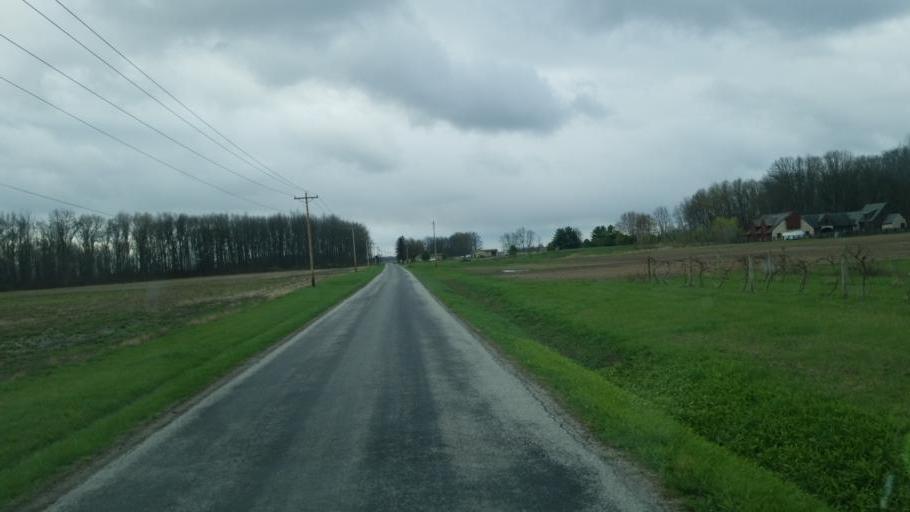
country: US
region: Ohio
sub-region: Delaware County
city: Ashley
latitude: 40.4070
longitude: -83.0018
